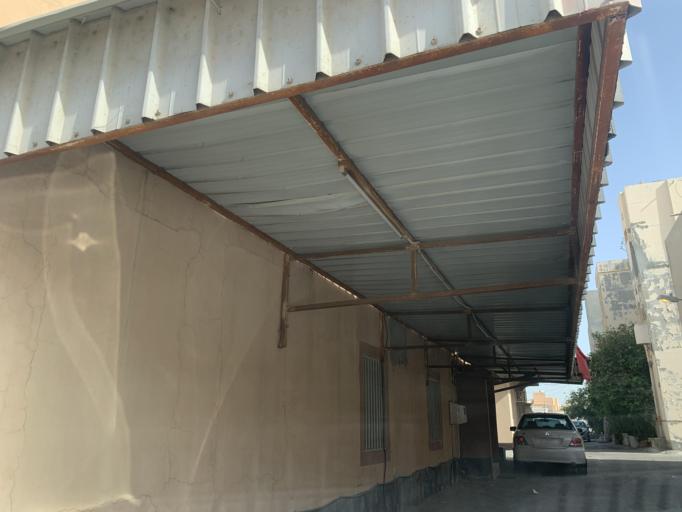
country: BH
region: Northern
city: Sitrah
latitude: 26.1638
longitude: 50.6131
